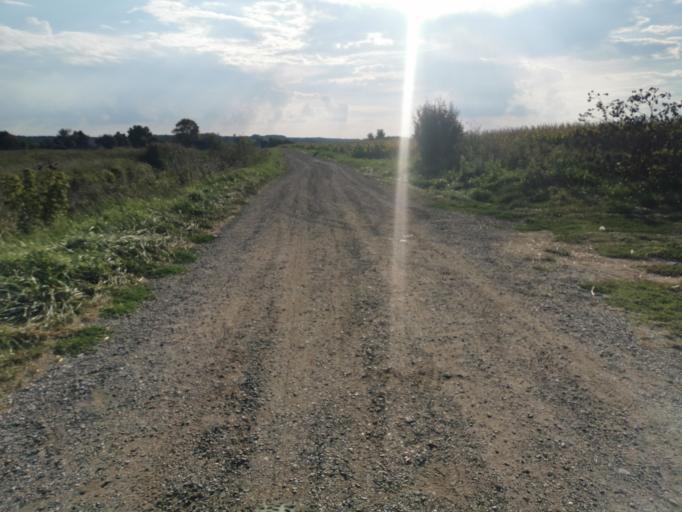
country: SK
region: Trnavsky
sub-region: Okres Senica
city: Senica
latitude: 48.6660
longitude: 17.2649
